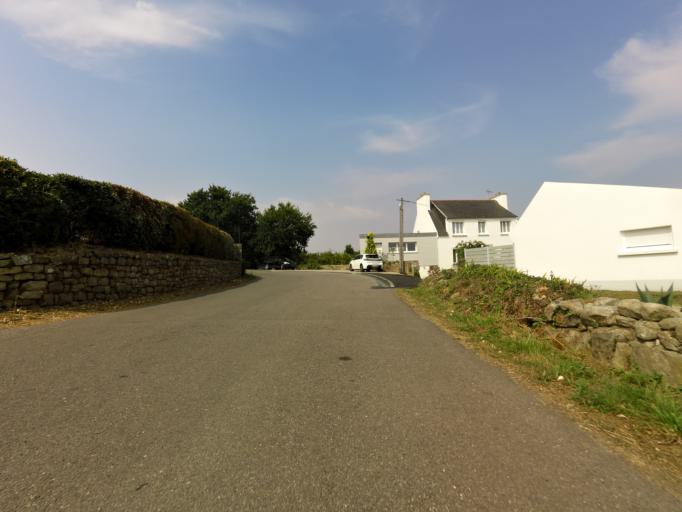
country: FR
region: Brittany
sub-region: Departement du Finistere
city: Esquibien
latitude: 48.0108
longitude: -4.5616
